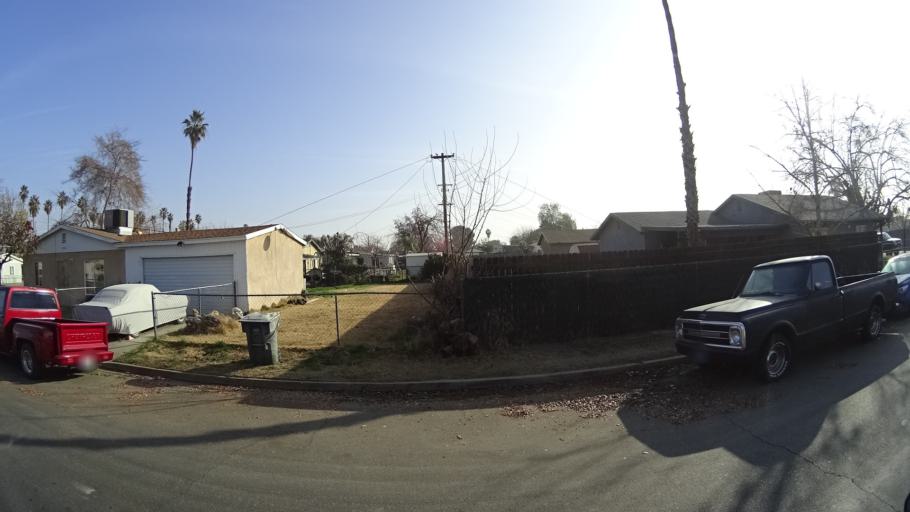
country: US
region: California
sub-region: Kern County
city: Bakersfield
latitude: 35.3352
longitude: -119.0337
